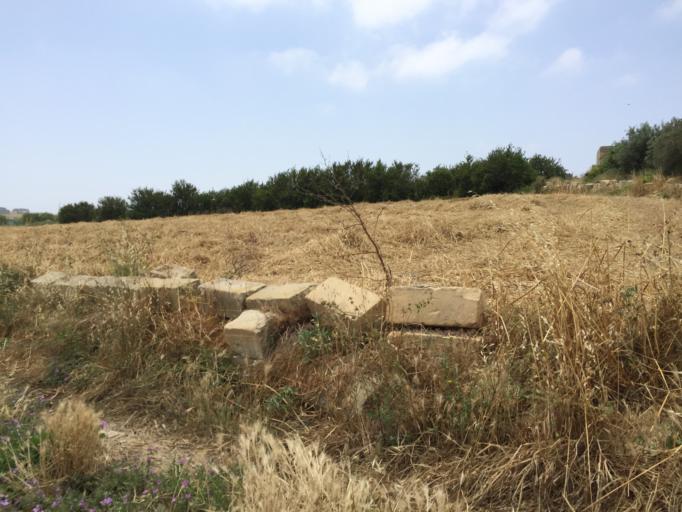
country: MT
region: L-Imtarfa
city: Imtarfa
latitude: 35.8883
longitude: 14.3803
